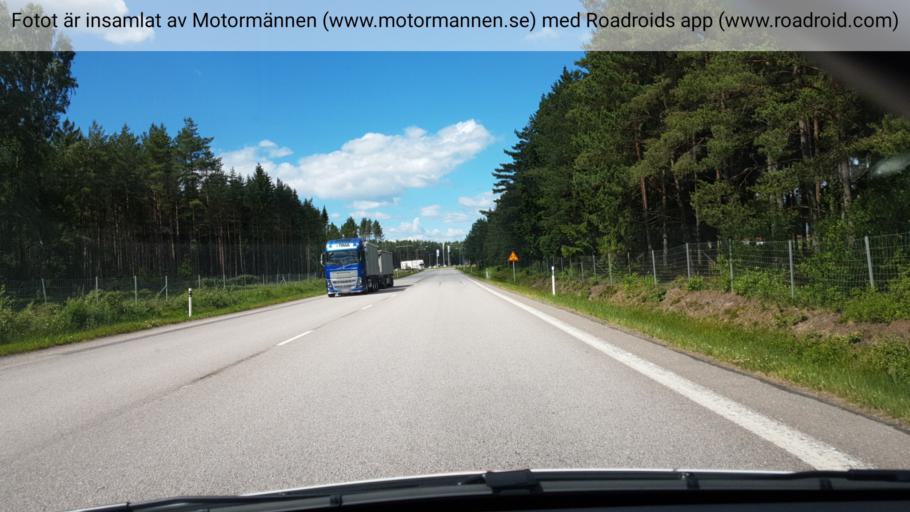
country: SE
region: Vaestra Goetaland
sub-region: Lidkopings Kommun
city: Lidkoping
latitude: 58.4861
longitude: 13.1911
